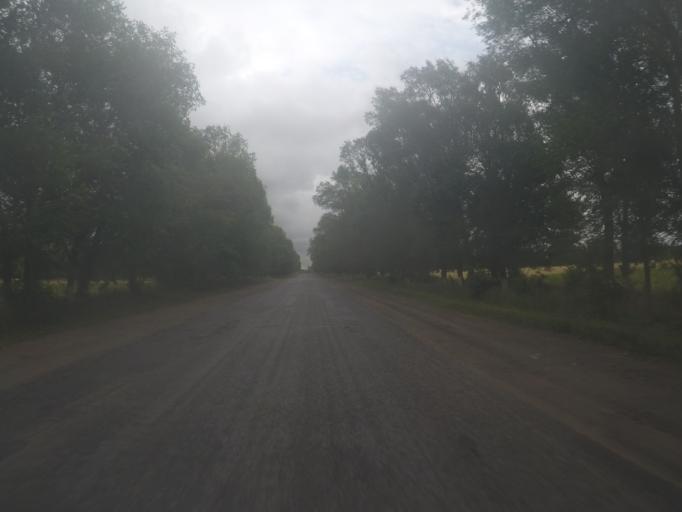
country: KG
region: Ysyk-Koel
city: Tyup
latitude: 42.7854
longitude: 78.2705
